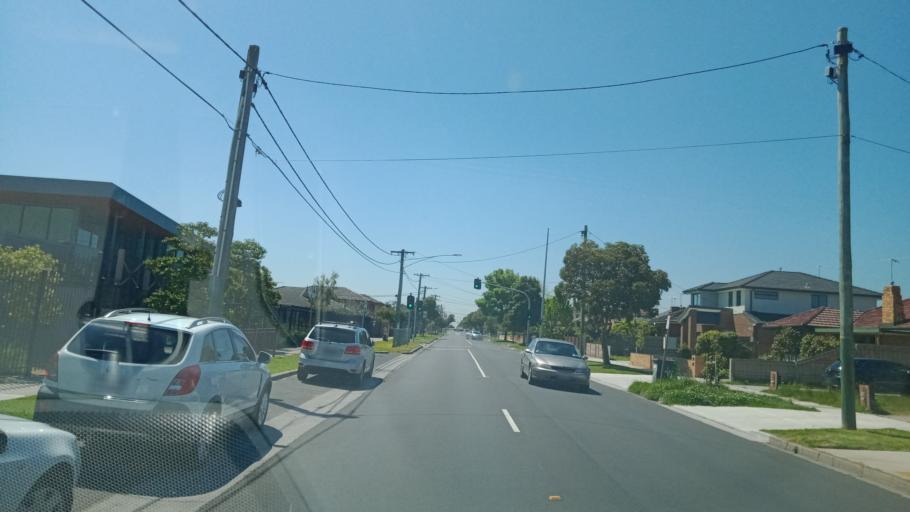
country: AU
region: Victoria
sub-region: Monash
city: Oakleigh South
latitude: -37.9203
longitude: 145.0738
